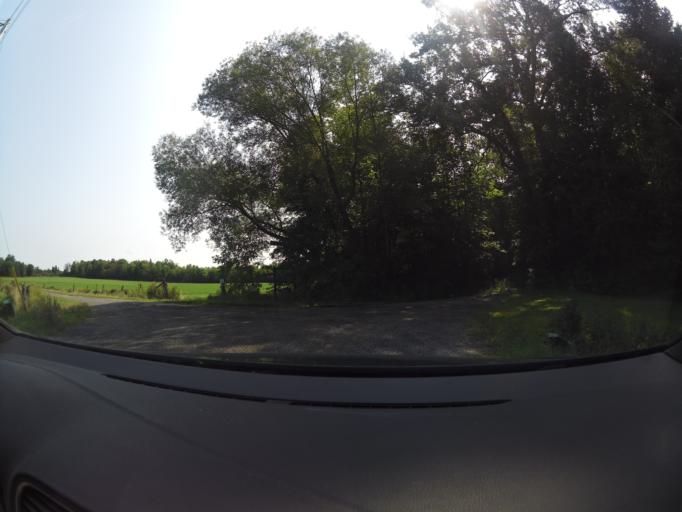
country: CA
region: Ontario
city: Arnprior
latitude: 45.4611
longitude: -76.1695
